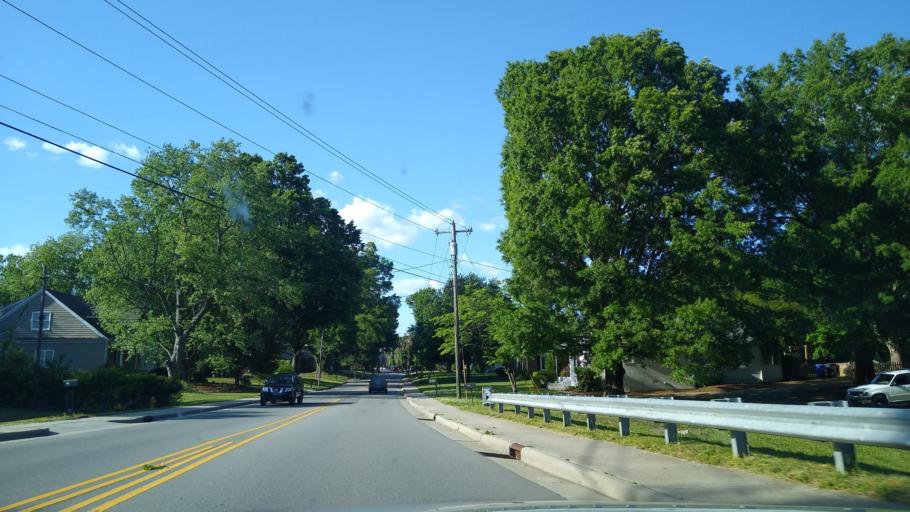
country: US
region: North Carolina
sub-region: Forsyth County
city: Kernersville
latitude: 36.1109
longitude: -80.0779
